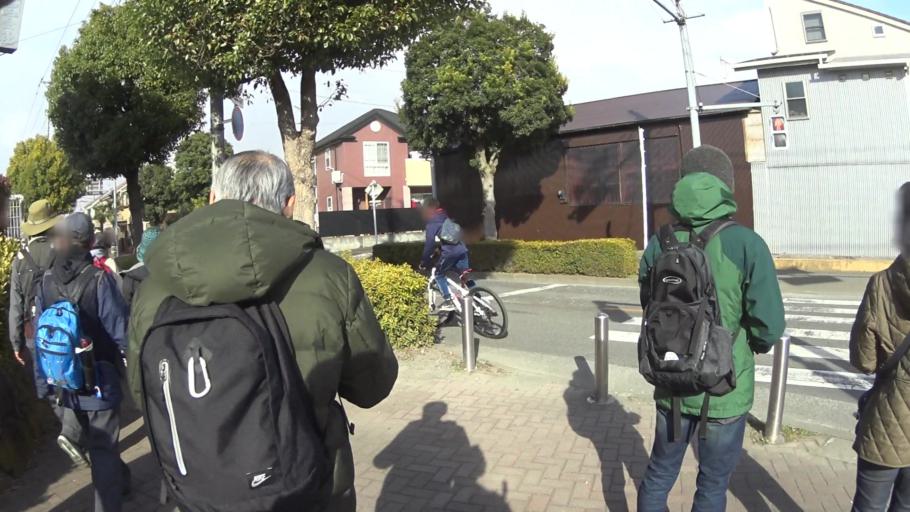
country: JP
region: Tokyo
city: Kokubunji
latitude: 35.6566
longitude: 139.4803
